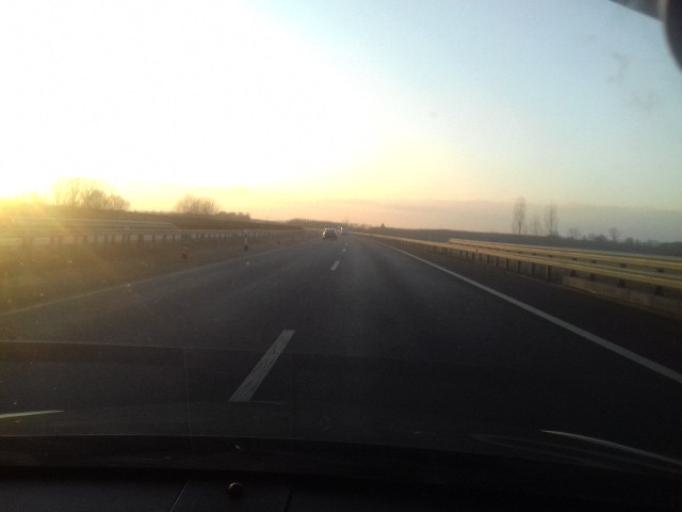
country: HU
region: Szabolcs-Szatmar-Bereg
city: Kalmanhaza
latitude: 47.9035
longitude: 21.5848
